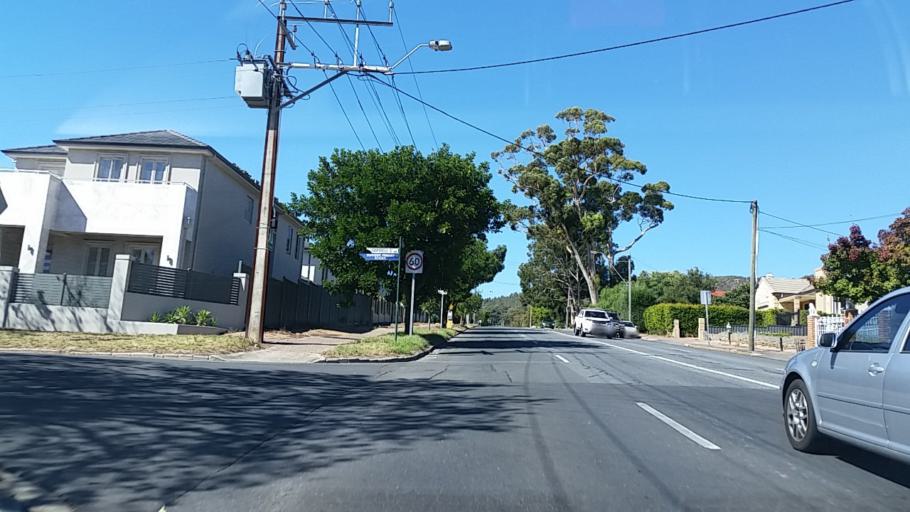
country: AU
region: South Australia
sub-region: Burnside
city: Hazelwood Park
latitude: -34.9381
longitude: 138.6624
